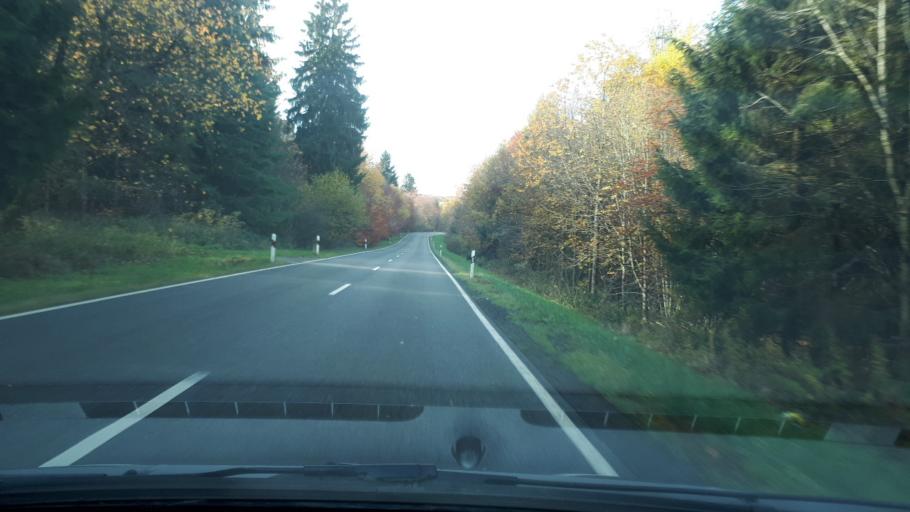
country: DE
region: Rheinland-Pfalz
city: Leienkaul
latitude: 50.2245
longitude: 7.0940
